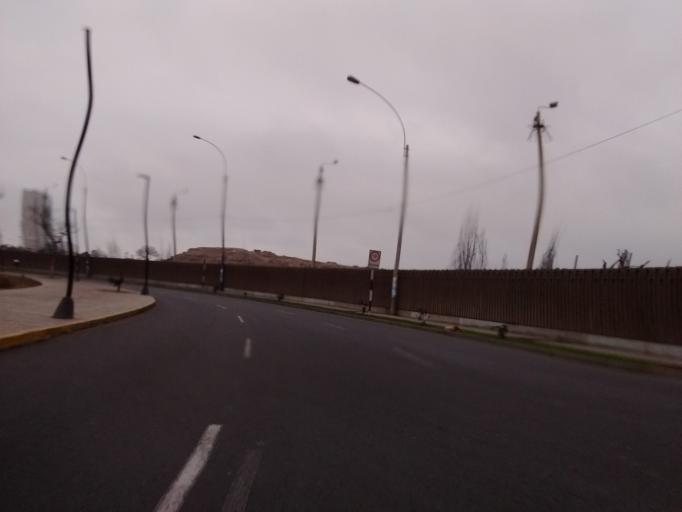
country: PE
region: Lima
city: Lima
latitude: -12.0670
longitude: -77.0618
